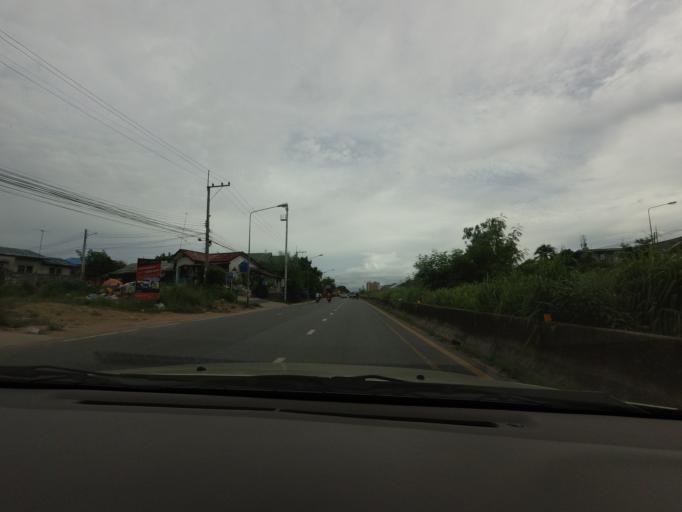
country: TH
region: Chon Buri
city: Phatthaya
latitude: 12.9195
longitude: 100.9026
